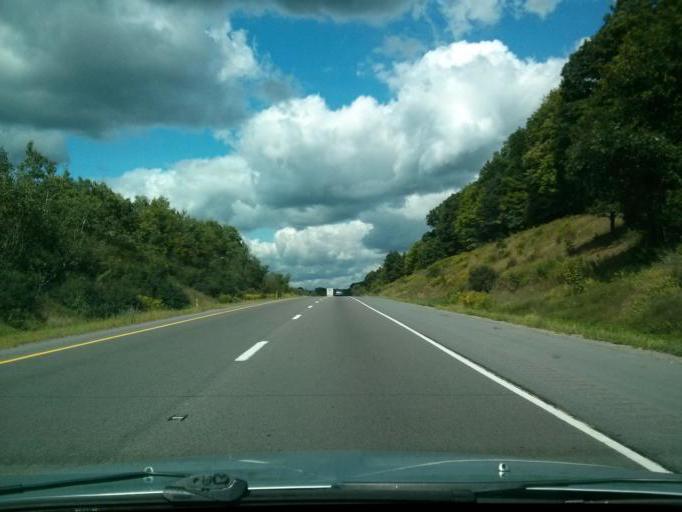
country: US
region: Pennsylvania
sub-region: Clearfield County
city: Treasure Lake
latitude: 41.1340
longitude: -78.7228
